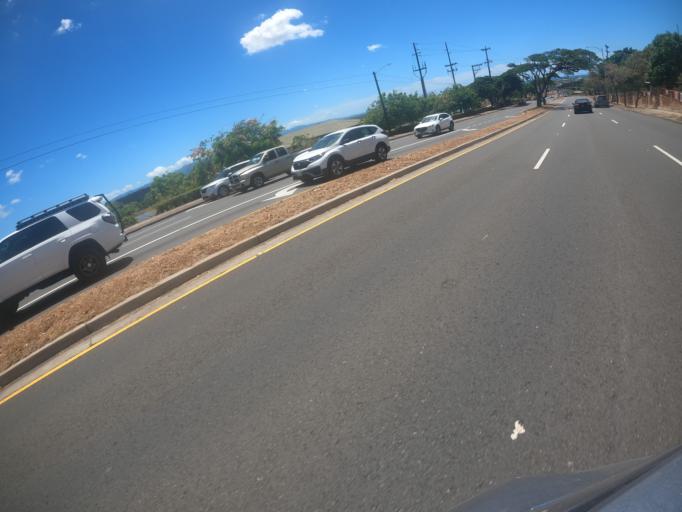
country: US
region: Hawaii
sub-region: Honolulu County
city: Makakilo City
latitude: 21.3441
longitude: -158.0796
